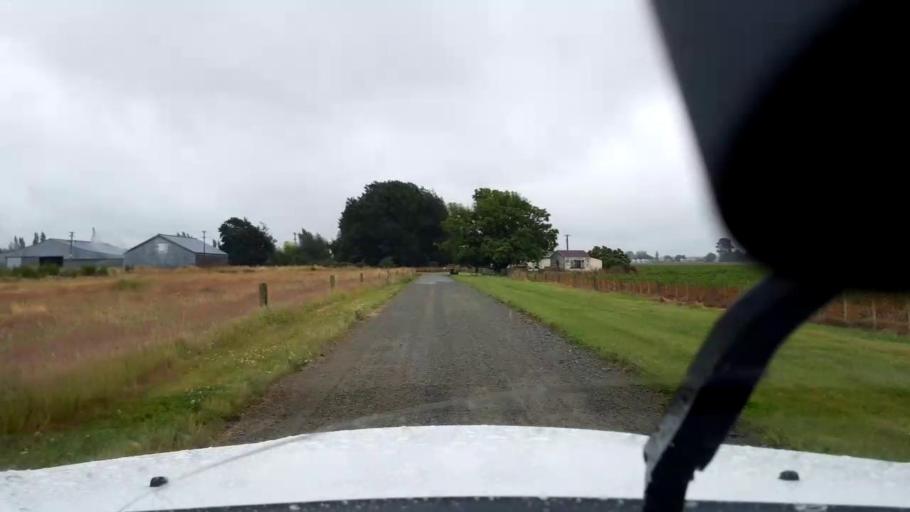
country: NZ
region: Canterbury
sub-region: Timaru District
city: Pleasant Point
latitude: -44.1887
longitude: 171.2817
